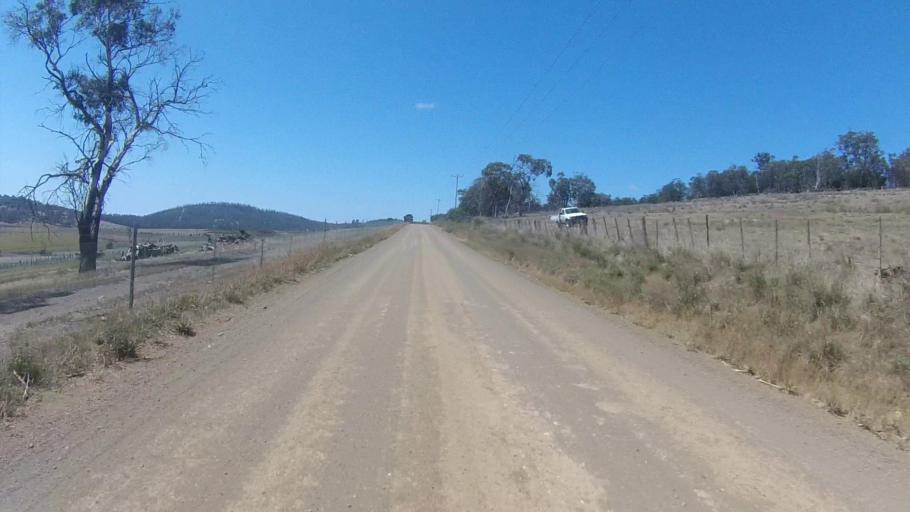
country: AU
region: Tasmania
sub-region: Sorell
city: Sorell
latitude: -42.8202
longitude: 147.6335
